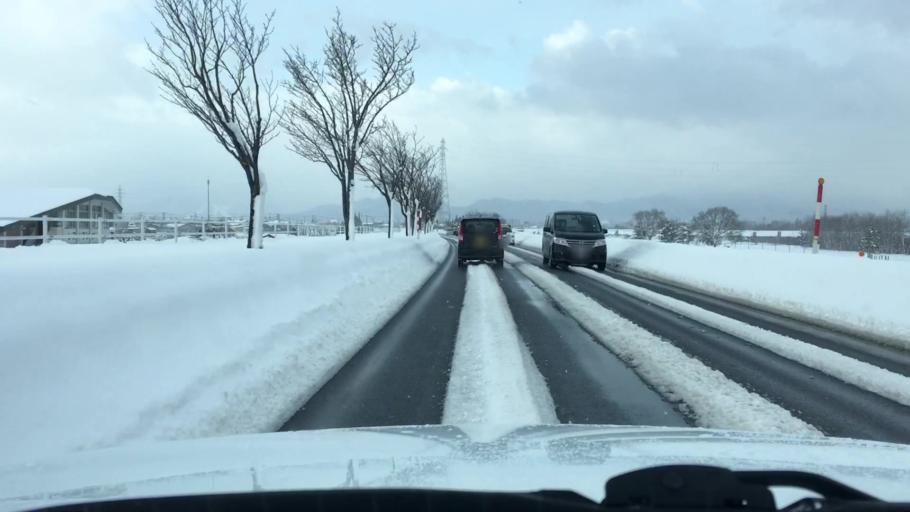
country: JP
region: Aomori
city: Hirosaki
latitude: 40.6323
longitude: 140.4729
